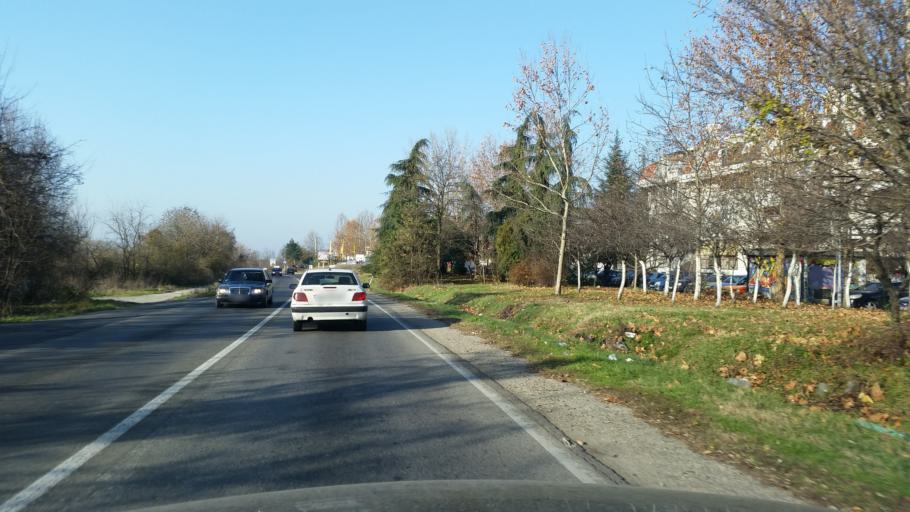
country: RS
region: Central Serbia
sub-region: Belgrade
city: Rakovica
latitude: 44.7374
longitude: 20.4179
